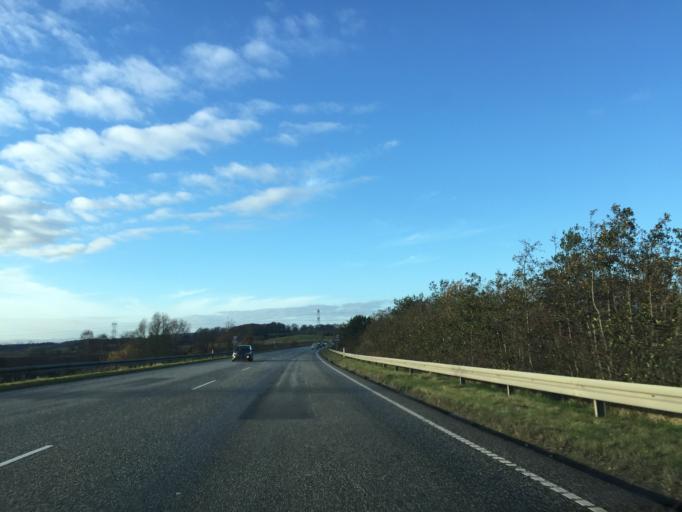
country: DK
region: Central Jutland
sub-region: Favrskov Kommune
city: Soften
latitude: 56.1880
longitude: 10.0823
